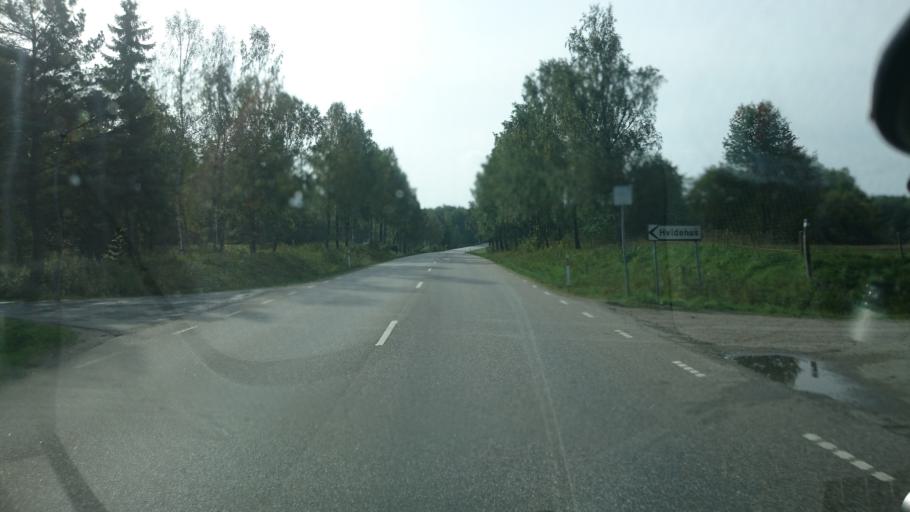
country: SE
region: Vaestra Goetaland
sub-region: Alingsas Kommun
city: Sollebrunn
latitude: 58.0725
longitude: 12.4817
